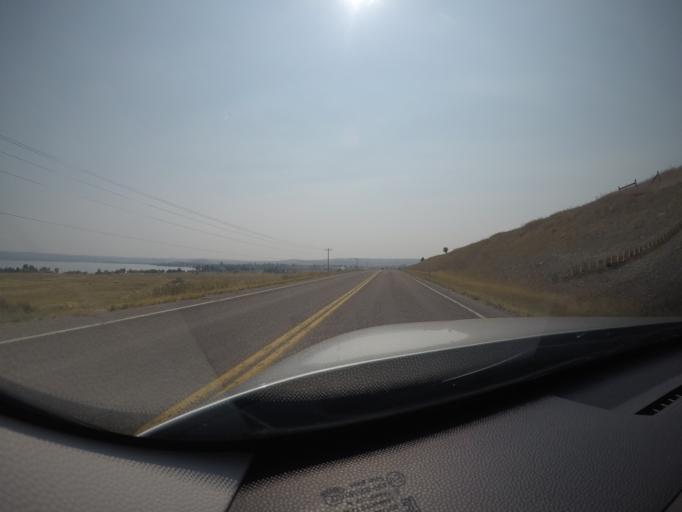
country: US
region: Montana
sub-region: Lake County
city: Polson
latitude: 47.7381
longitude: -114.1831
